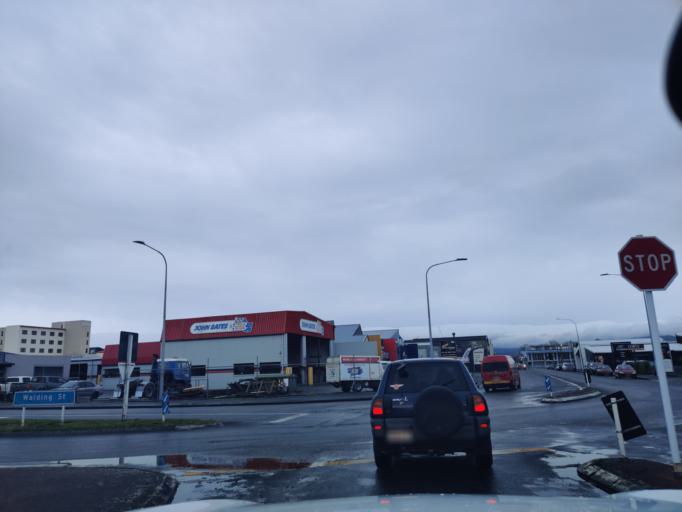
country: NZ
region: Manawatu-Wanganui
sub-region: Palmerston North City
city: Palmerston North
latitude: -40.3550
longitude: 175.6040
